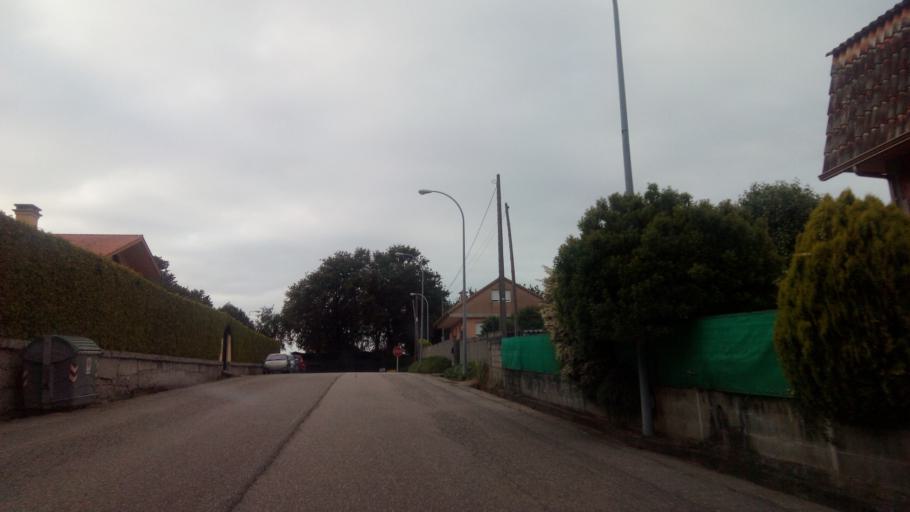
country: ES
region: Galicia
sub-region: Provincia de Pontevedra
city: Nigran
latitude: 42.1227
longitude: -8.8020
